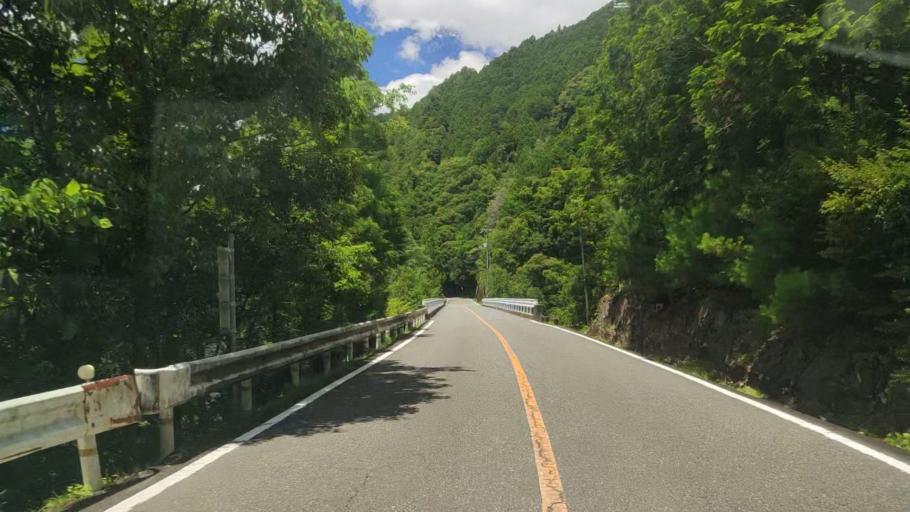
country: JP
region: Mie
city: Owase
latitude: 33.9972
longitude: 136.0233
